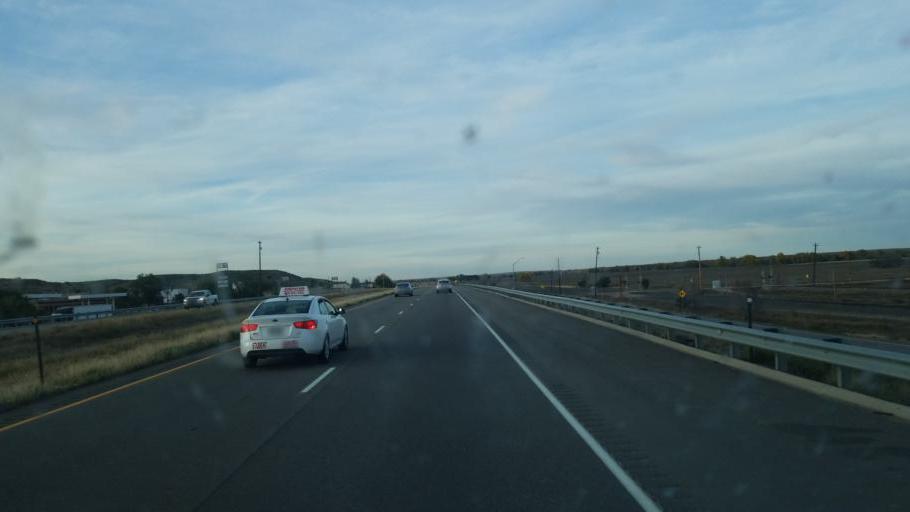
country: US
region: Colorado
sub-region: Pueblo County
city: Pueblo West
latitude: 38.4308
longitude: -104.6071
